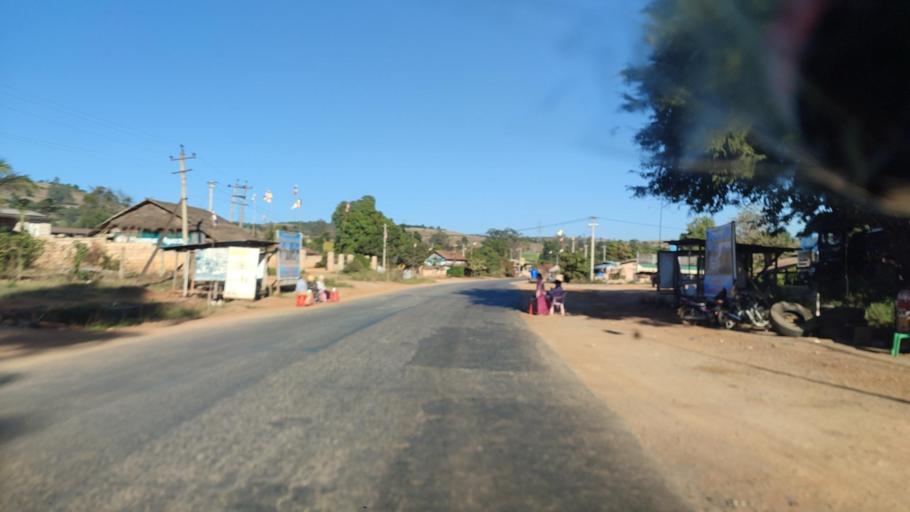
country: MM
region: Mandalay
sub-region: Pyin Oo Lwin District
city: Pyin Oo Lwin
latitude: 22.3574
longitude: 96.8767
